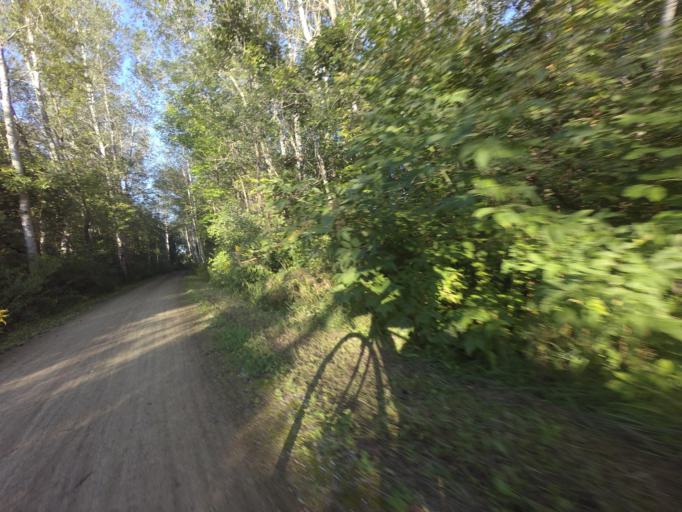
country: CA
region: Ontario
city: Orangeville
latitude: 43.8231
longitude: -79.9193
